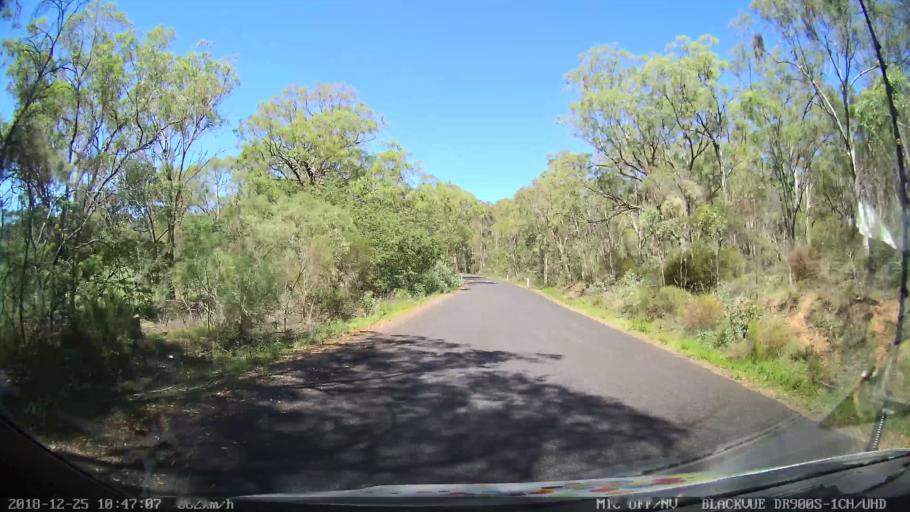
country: AU
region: New South Wales
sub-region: Upper Hunter Shire
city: Merriwa
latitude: -32.4460
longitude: 150.2790
